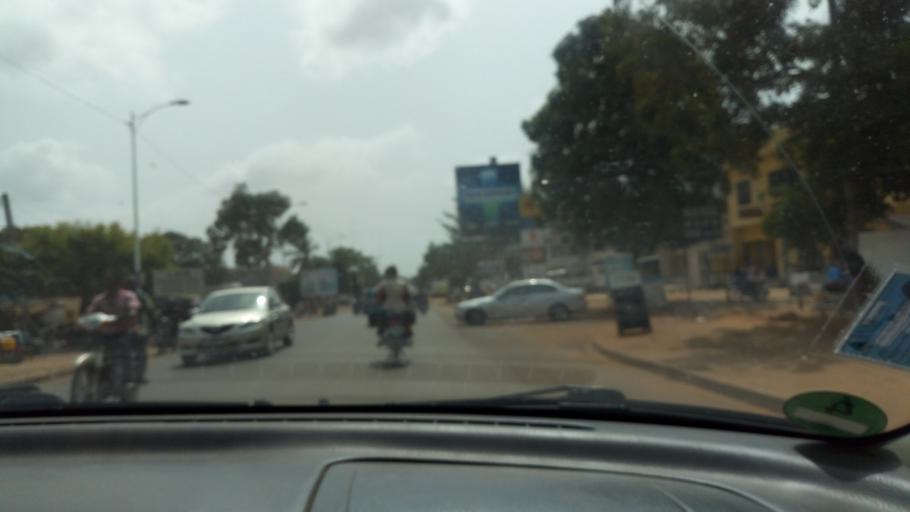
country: TG
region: Maritime
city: Lome
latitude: 6.1804
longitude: 1.1719
